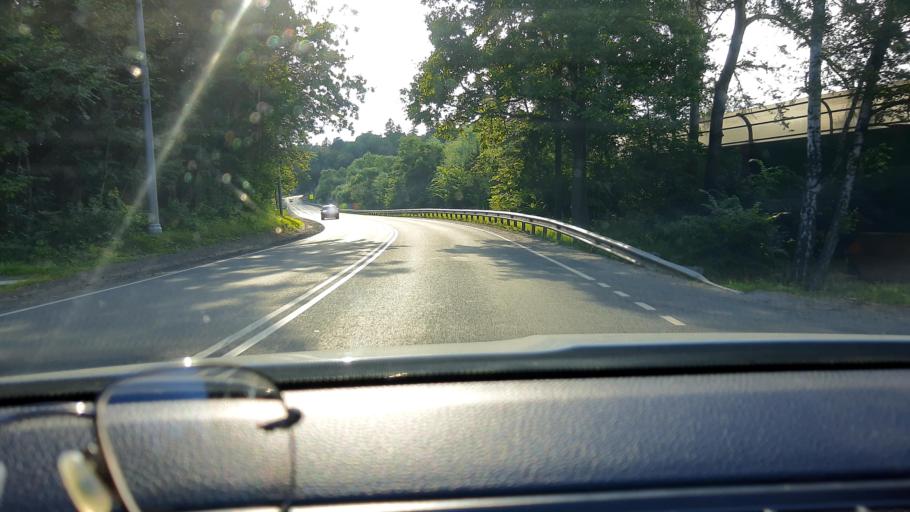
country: RU
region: Moskovskaya
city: Nikolina Gora
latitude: 55.7058
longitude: 37.0538
